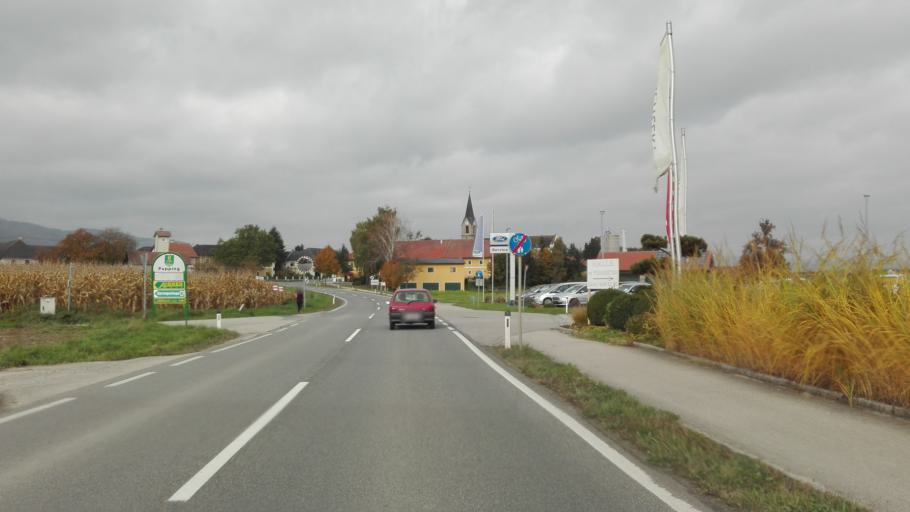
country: AT
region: Upper Austria
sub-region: Politischer Bezirk Urfahr-Umgebung
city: Feldkirchen an der Donau
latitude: 48.3355
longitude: 14.0023
